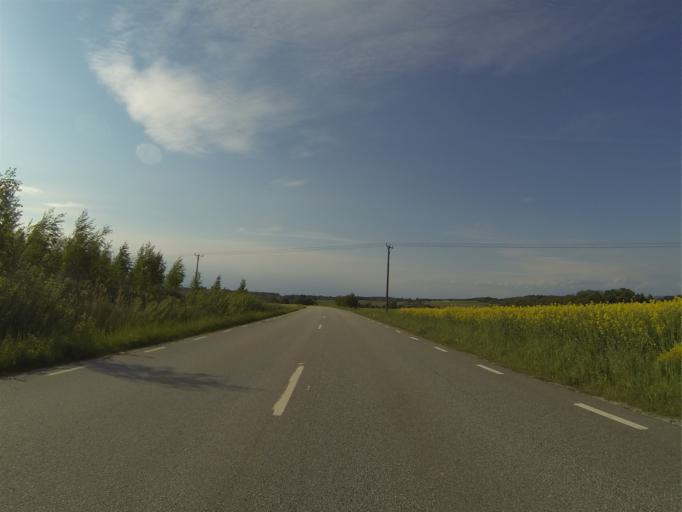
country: SE
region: Skane
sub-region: Lunds Kommun
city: Lund
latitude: 55.7055
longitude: 13.3025
